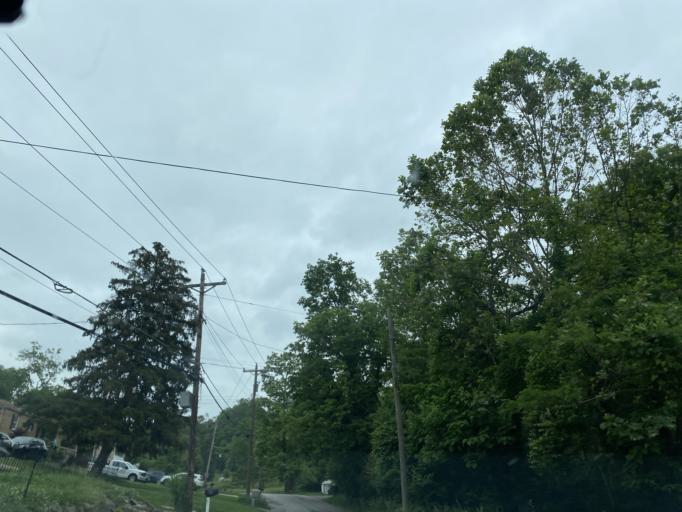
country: US
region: Kentucky
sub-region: Campbell County
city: Bellevue
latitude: 39.0996
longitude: -84.4703
